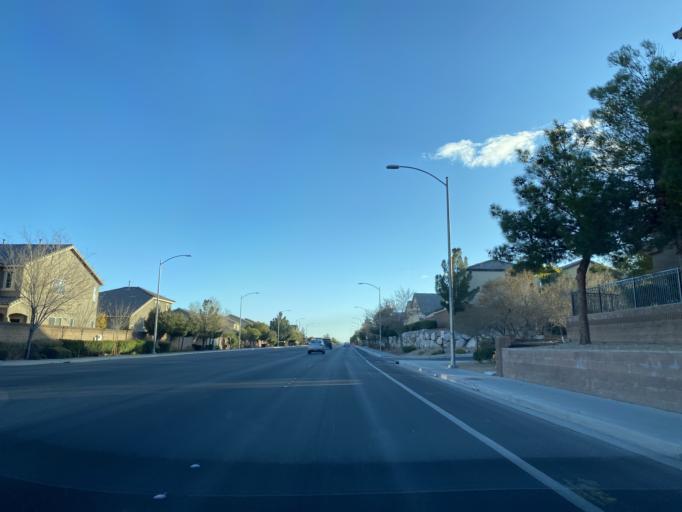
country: US
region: Nevada
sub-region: Clark County
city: Summerlin South
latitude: 36.3053
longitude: -115.3059
